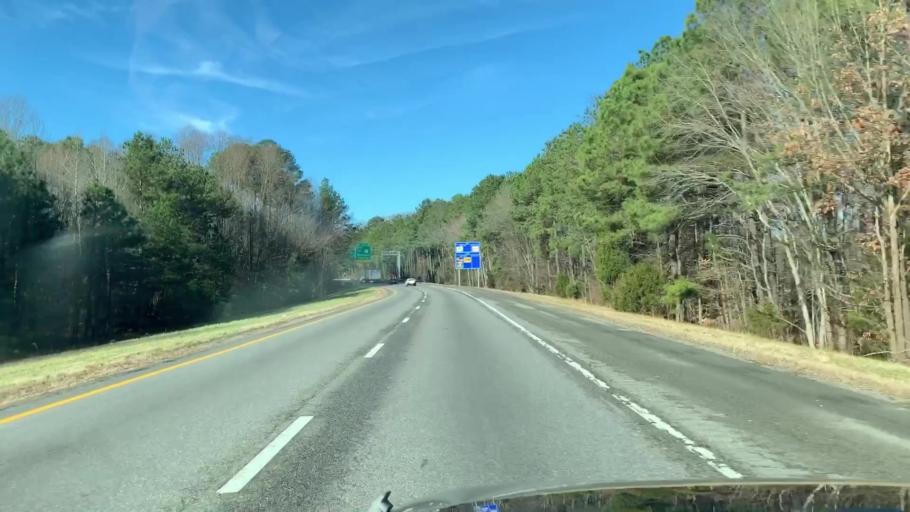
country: US
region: Virginia
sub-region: Henrico County
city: Chamberlayne
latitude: 37.6560
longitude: -77.4404
